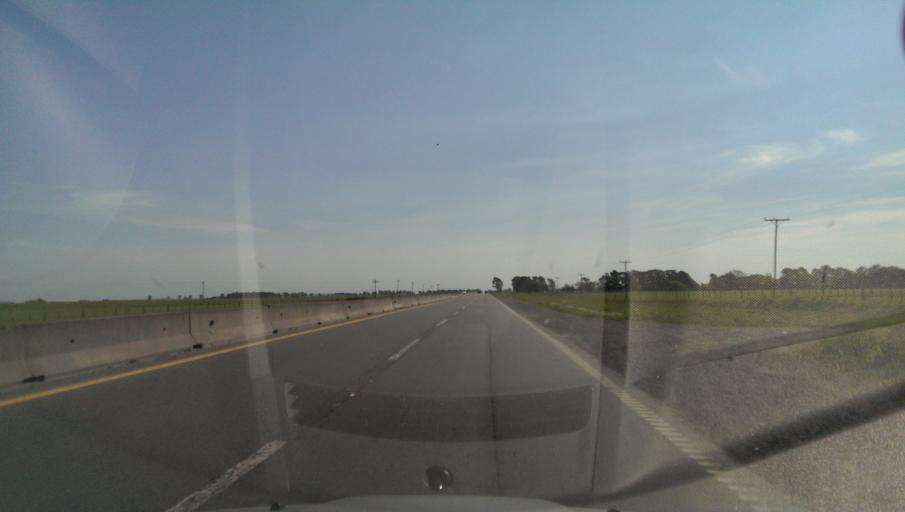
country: AR
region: Buenos Aires
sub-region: Partido de Azul
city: Azul
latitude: -36.8442
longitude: -59.9135
